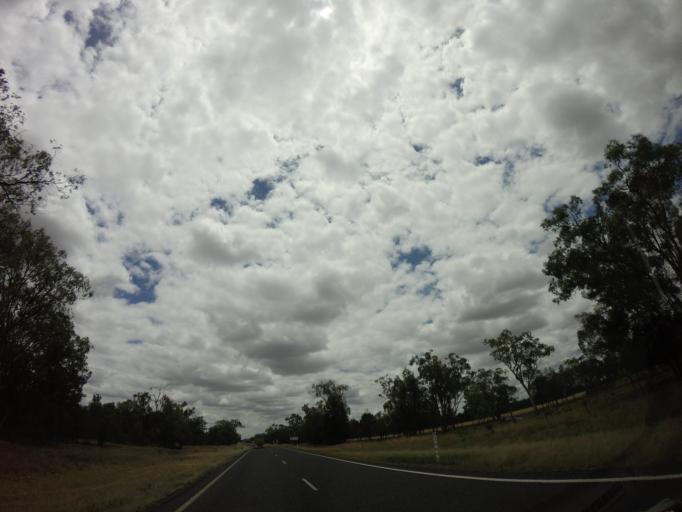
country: AU
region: Queensland
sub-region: Goondiwindi
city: Goondiwindi
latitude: -28.4489
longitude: 150.2990
